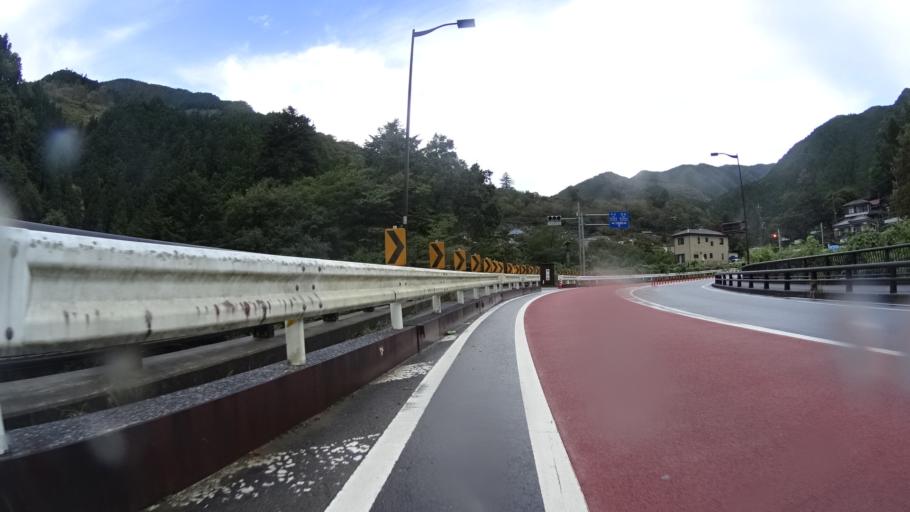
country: JP
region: Tokyo
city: Itsukaichi
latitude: 35.8005
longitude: 139.0912
